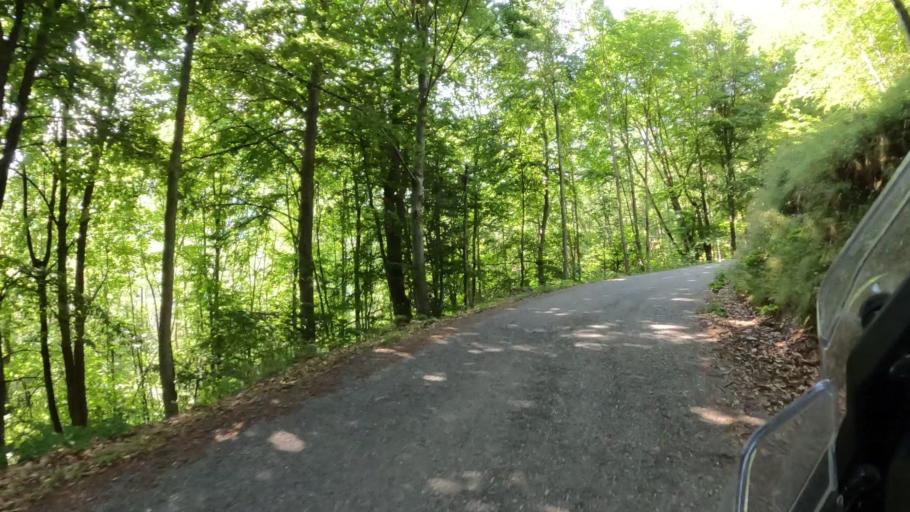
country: IT
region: Piedmont
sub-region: Provincia di Torino
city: Lemie
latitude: 45.2171
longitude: 7.3133
